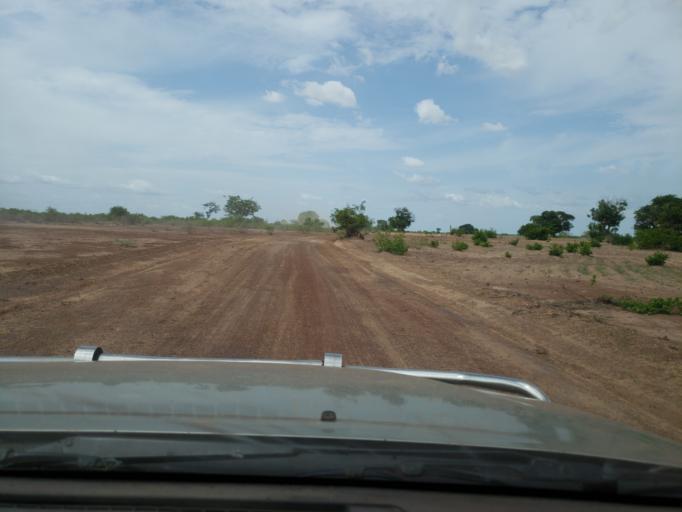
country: ML
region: Segou
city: Bla
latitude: 12.7396
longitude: -5.6511
